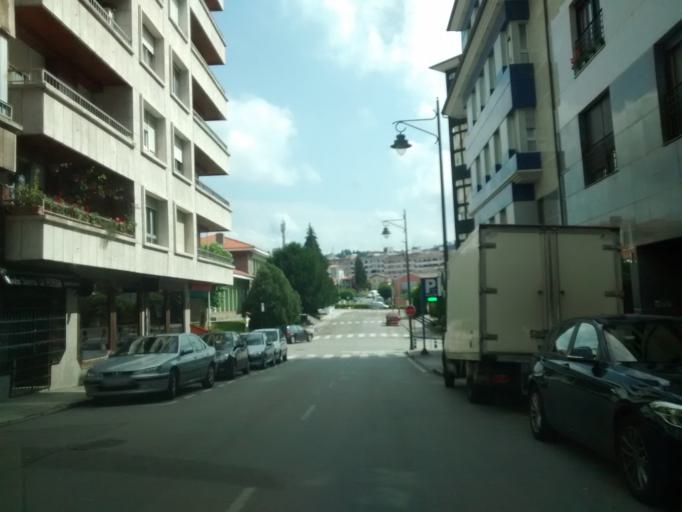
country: ES
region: Asturias
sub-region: Province of Asturias
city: Pola de Siero
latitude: 43.3933
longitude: -5.6587
